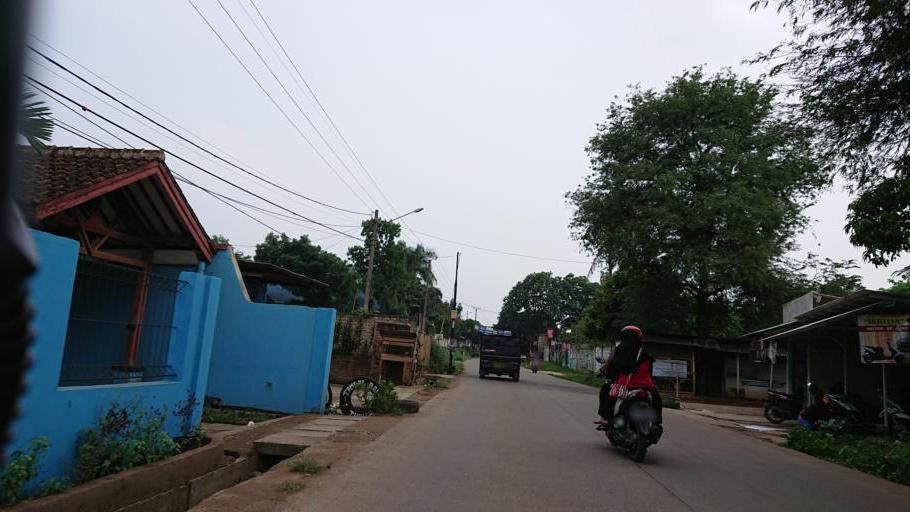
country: ID
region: West Java
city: Parung
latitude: -6.3993
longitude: 106.6887
